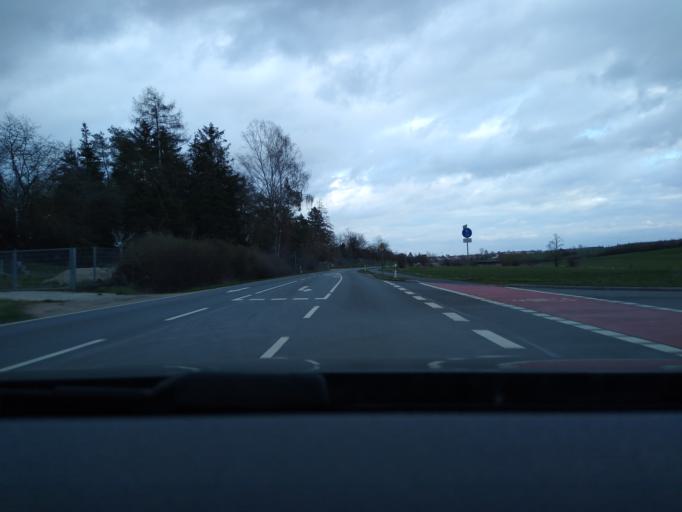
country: DE
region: Bavaria
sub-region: Regierungsbezirk Mittelfranken
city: Zirndorf
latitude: 49.4479
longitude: 10.9288
